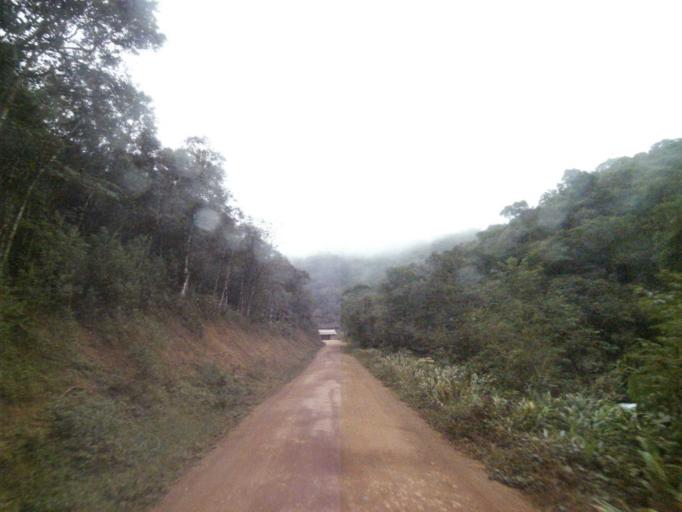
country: BR
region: Santa Catarina
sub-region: Anitapolis
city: Anitapolis
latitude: -27.8962
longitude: -49.1299
